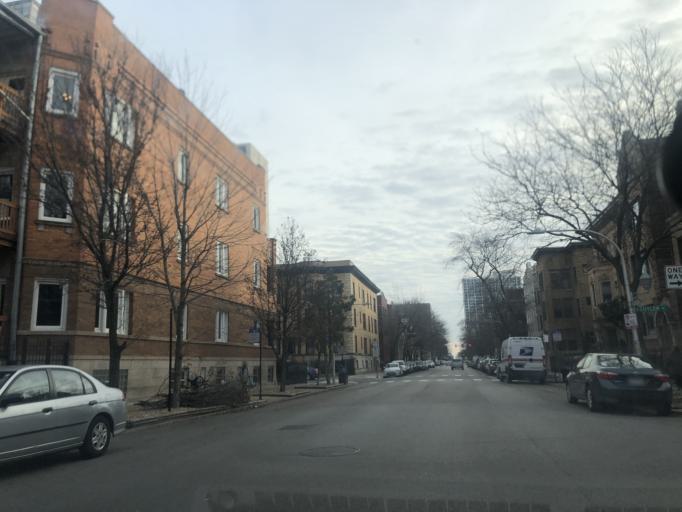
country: US
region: Illinois
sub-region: Cook County
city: Lincolnwood
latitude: 41.9562
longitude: -87.6497
